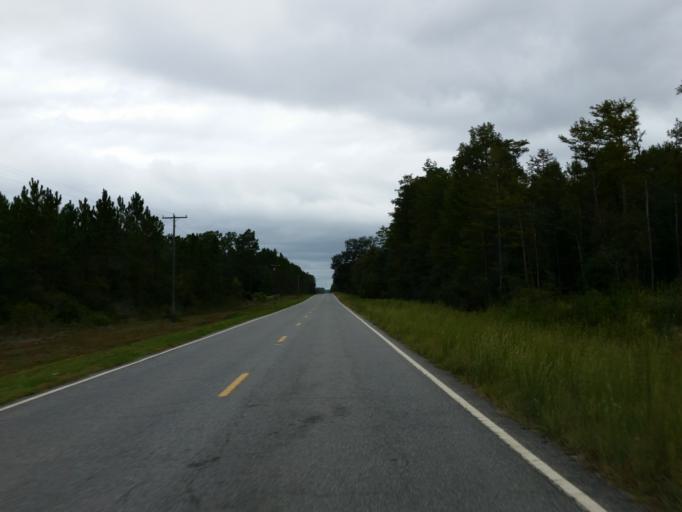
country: US
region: Georgia
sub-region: Echols County
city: Statenville
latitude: 30.8764
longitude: -83.0021
